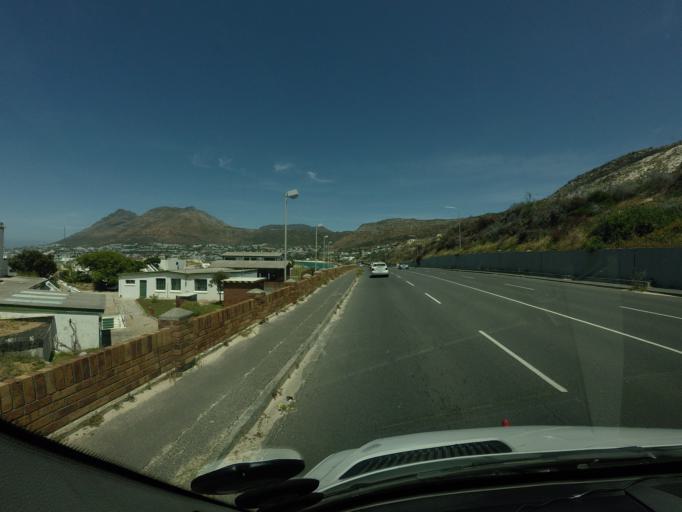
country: ZA
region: Western Cape
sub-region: City of Cape Town
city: Retreat
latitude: -34.1776
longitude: 18.4265
